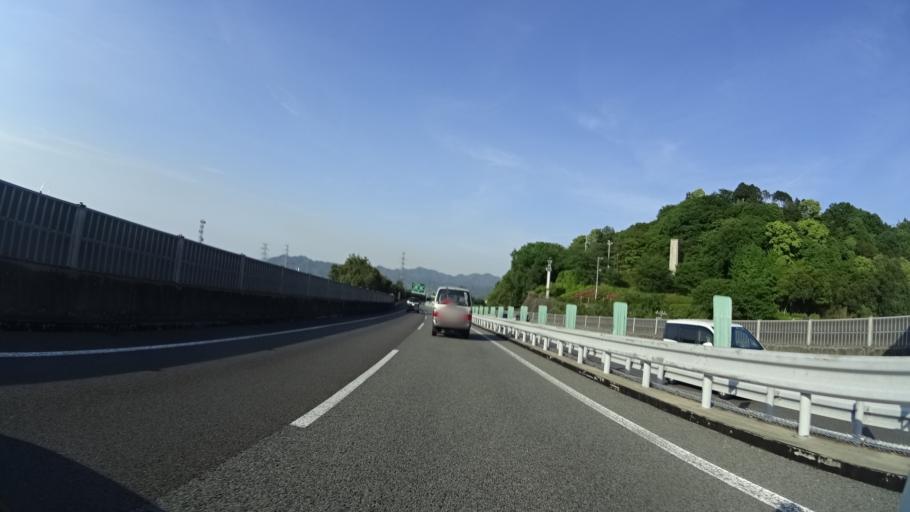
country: JP
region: Ehime
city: Kawanoecho
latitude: 33.9715
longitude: 133.5557
